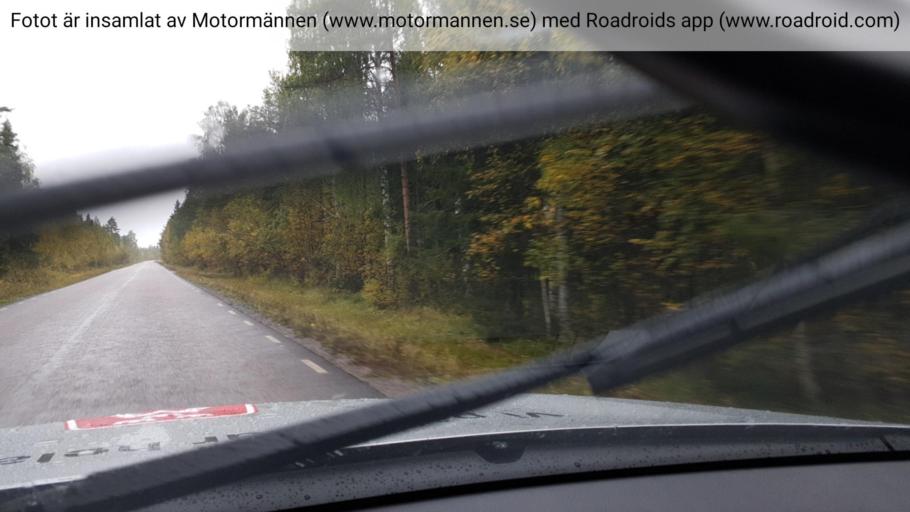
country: SE
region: Norrbotten
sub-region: Lulea Kommun
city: Gammelstad
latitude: 65.7286
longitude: 22.1275
